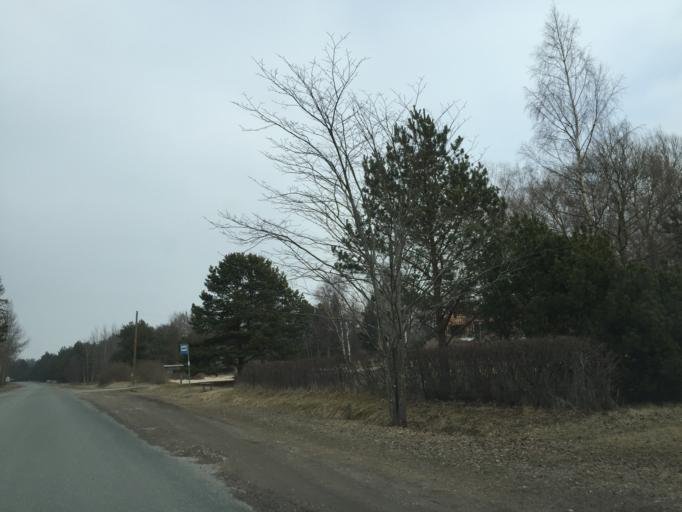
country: LV
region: Salacgrivas
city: Ainazi
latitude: 58.0086
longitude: 24.4472
